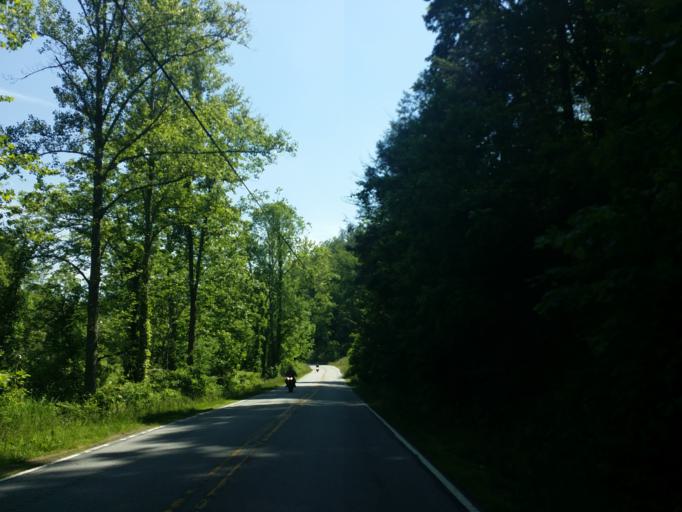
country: US
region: North Carolina
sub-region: Madison County
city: Marshall
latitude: 35.7026
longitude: -82.7557
